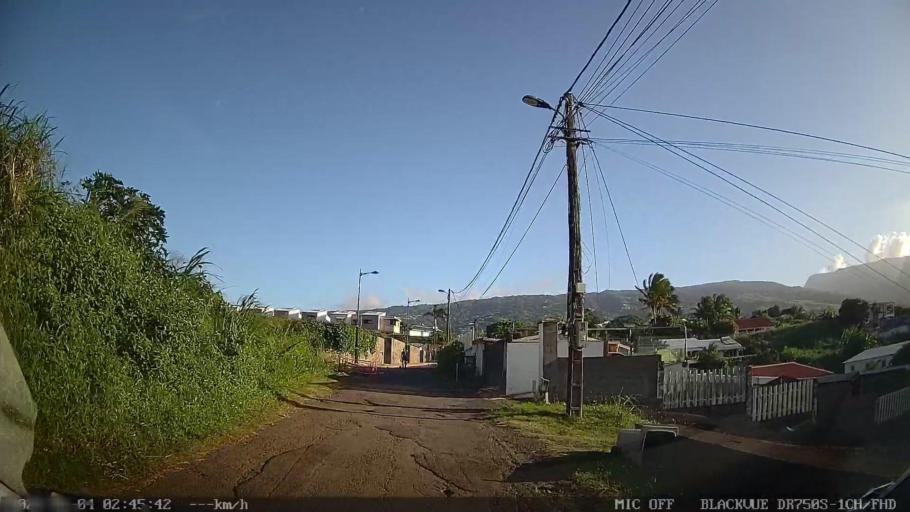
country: RE
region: Reunion
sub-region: Reunion
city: Sainte-Marie
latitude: -20.9205
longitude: 55.5250
